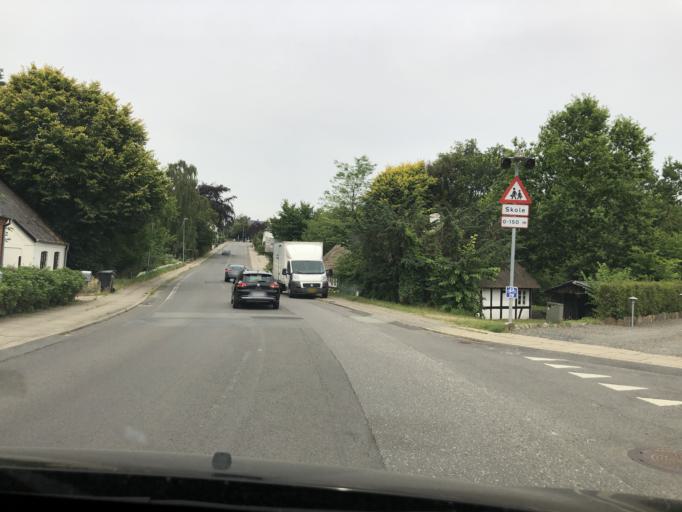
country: DK
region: South Denmark
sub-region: Assens Kommune
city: Glamsbjerg
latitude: 55.2683
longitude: 10.1156
